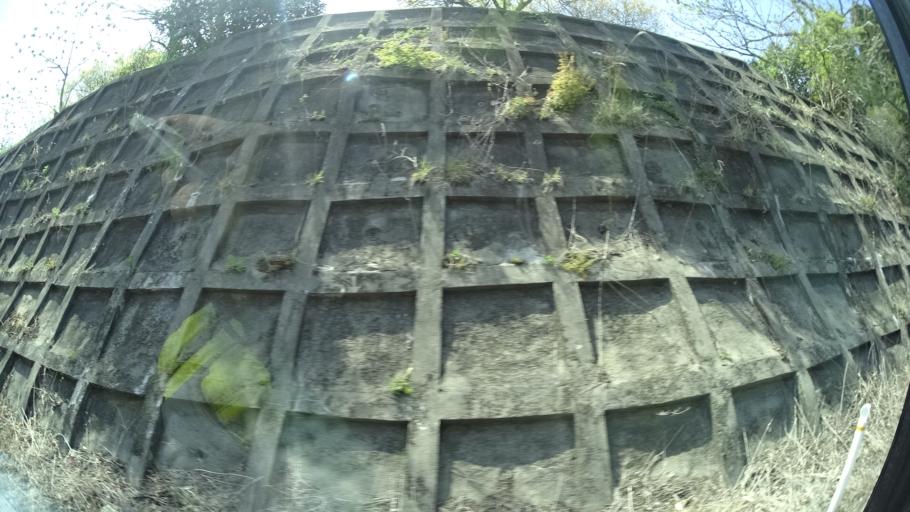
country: JP
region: Iwate
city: Ofunato
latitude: 39.0006
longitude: 141.7101
